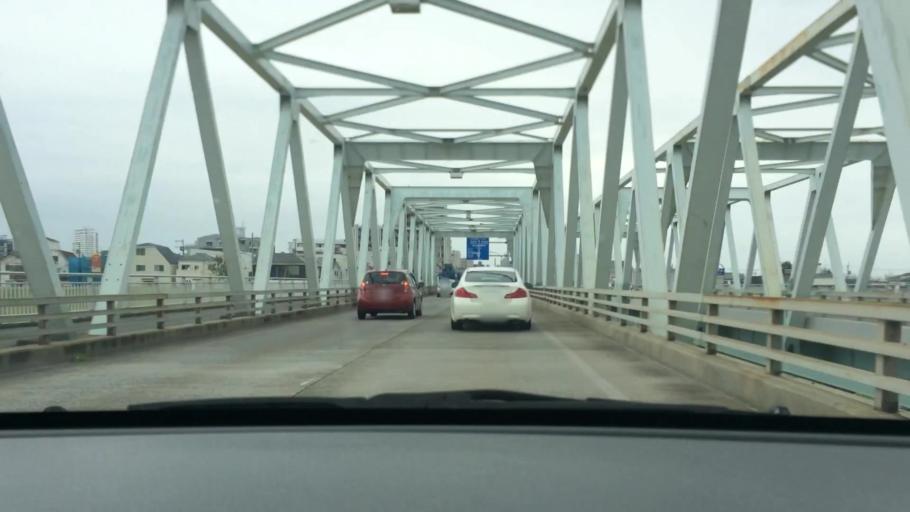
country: JP
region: Chiba
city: Matsudo
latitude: 35.7348
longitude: 139.8979
